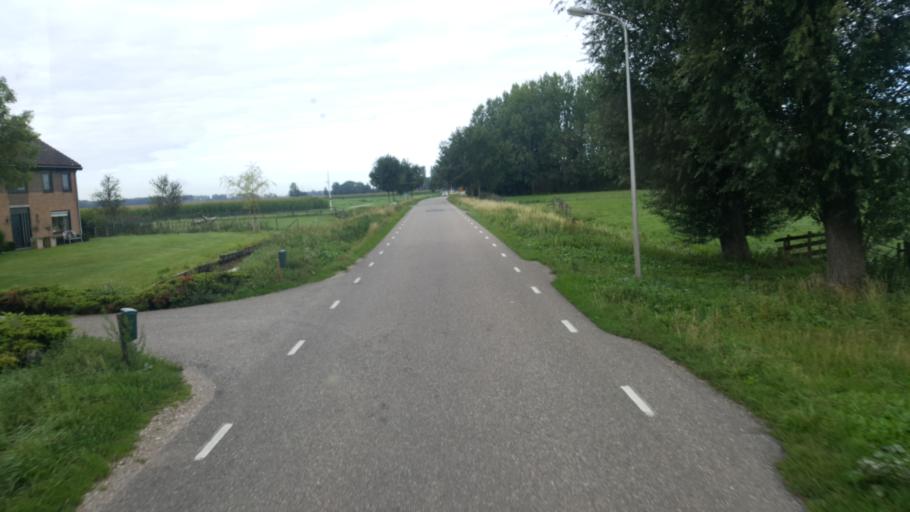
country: NL
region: South Holland
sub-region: Gemeente Hardinxveld-Giessendam
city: Neder-Hardinxveld
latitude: 51.8676
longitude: 4.8374
